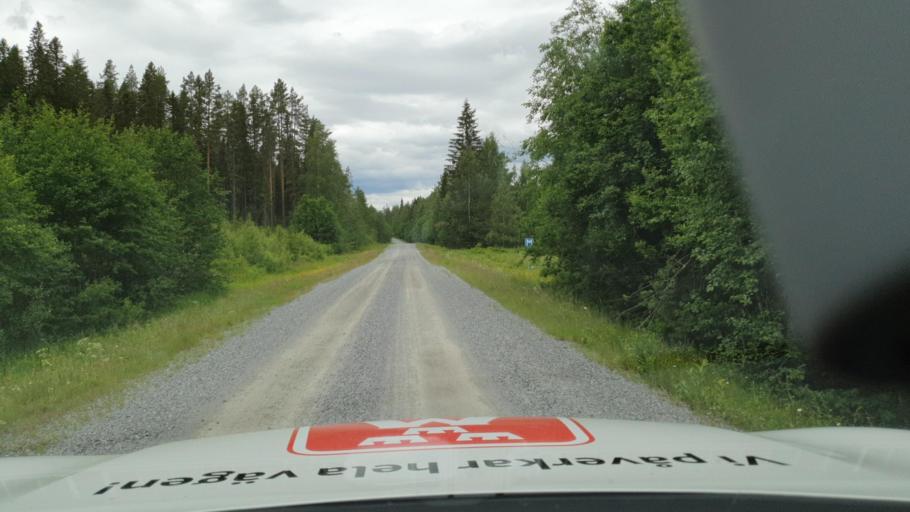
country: SE
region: Vaesterbotten
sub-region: Nordmalings Kommun
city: Nordmaling
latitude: 63.7343
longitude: 19.4203
